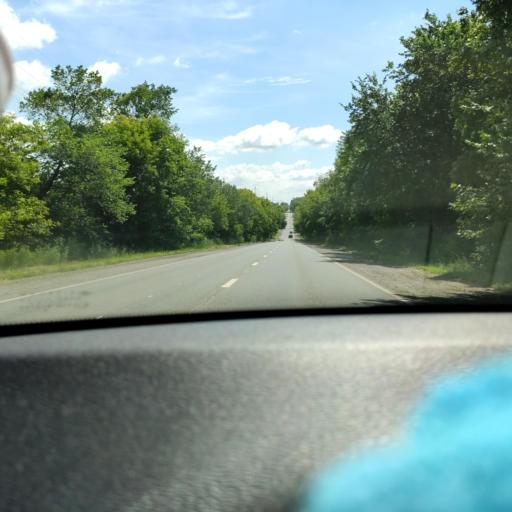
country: RU
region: Samara
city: Novosemeykino
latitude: 53.3226
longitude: 50.2645
